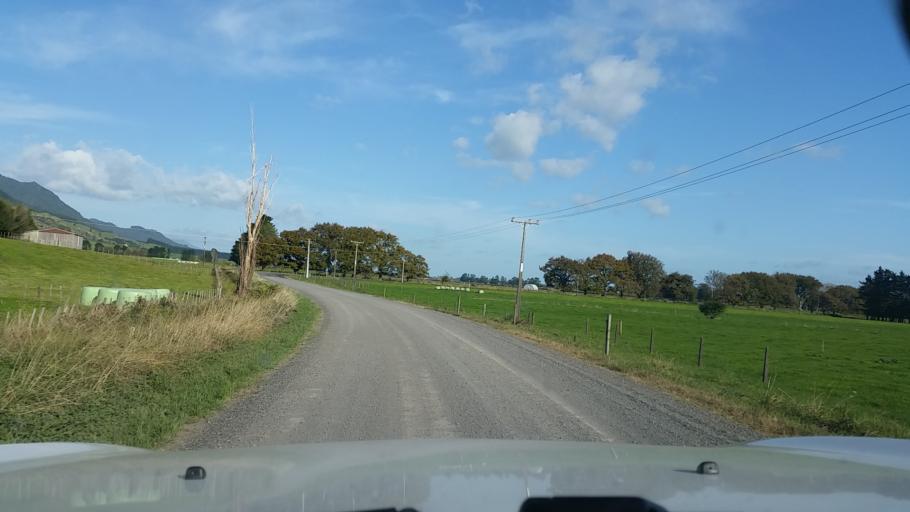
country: NZ
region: Bay of Plenty
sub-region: Western Bay of Plenty District
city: Katikati
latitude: -37.6140
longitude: 175.7956
